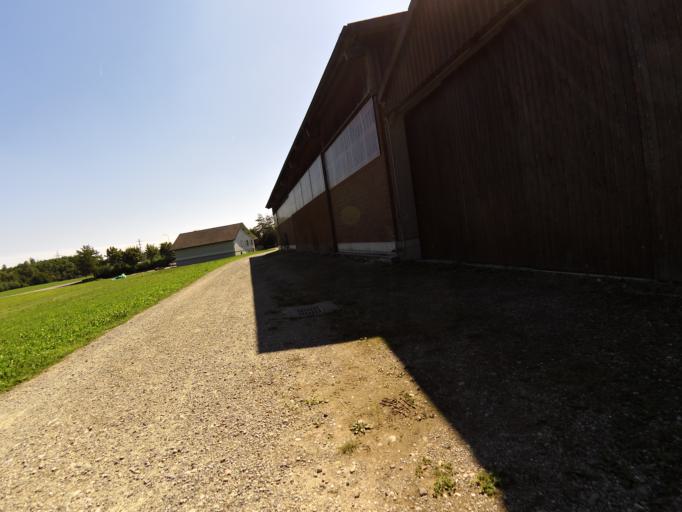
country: CH
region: Thurgau
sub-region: Kreuzlingen District
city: Tagerwilen
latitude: 47.6265
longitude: 9.1343
